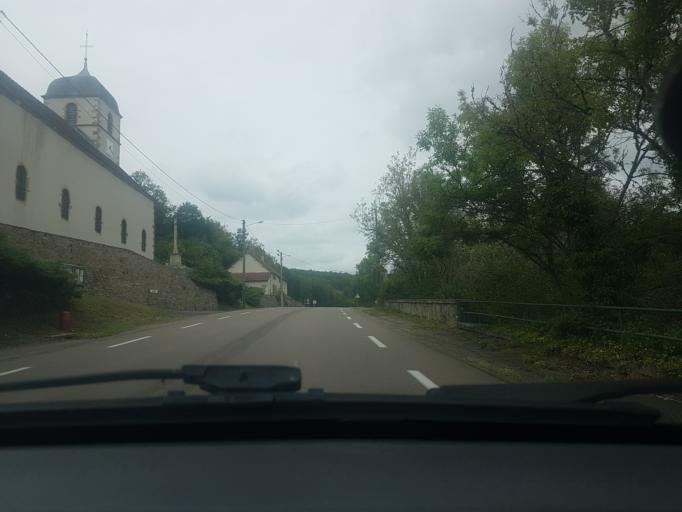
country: FR
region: Bourgogne
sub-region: Departement de la Cote-d'Or
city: Arnay-le-Duc
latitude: 47.1540
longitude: 4.4456
